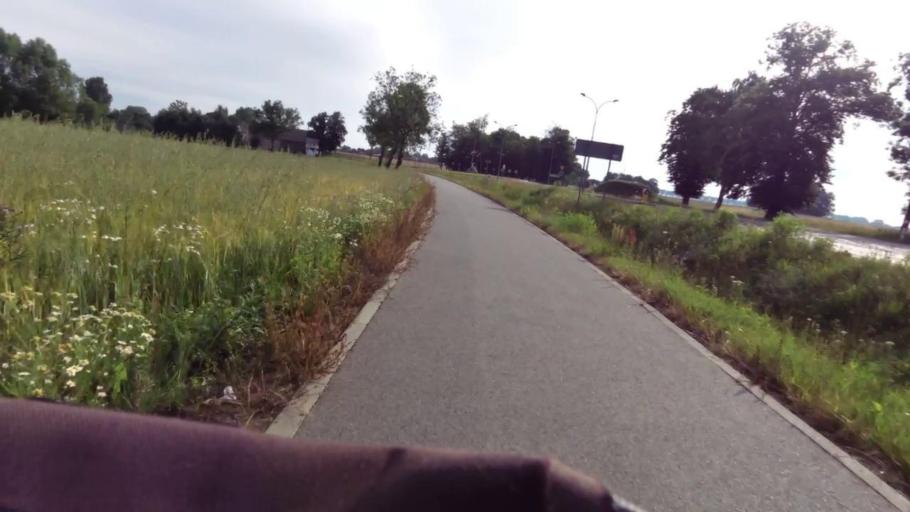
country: PL
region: West Pomeranian Voivodeship
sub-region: Powiat kamienski
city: Kamien Pomorski
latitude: 53.9928
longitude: 14.8149
